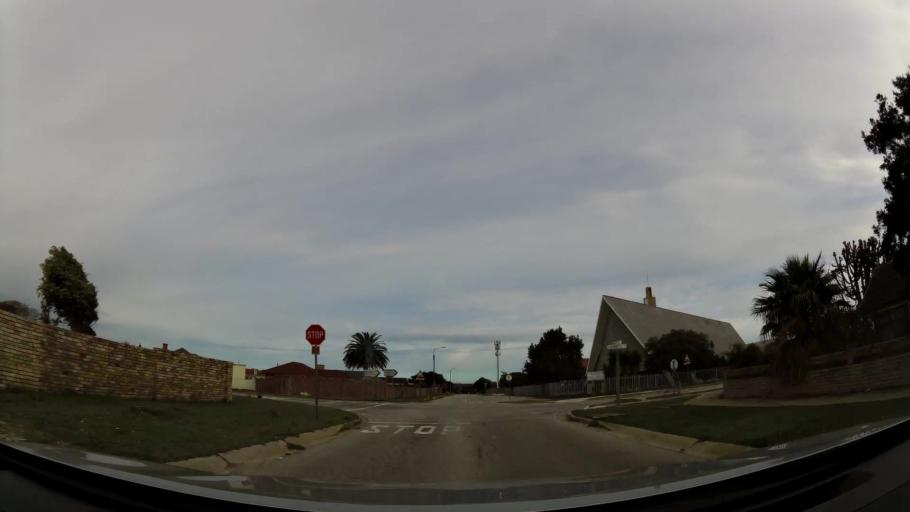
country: ZA
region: Eastern Cape
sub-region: Nelson Mandela Bay Metropolitan Municipality
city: Port Elizabeth
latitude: -33.9426
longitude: 25.4949
